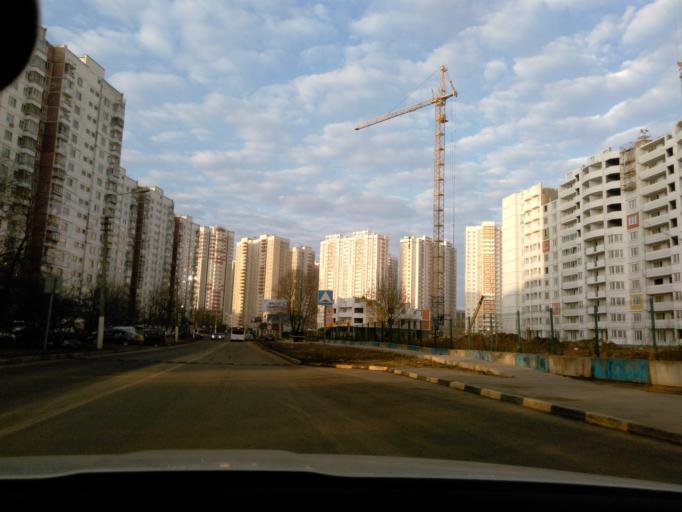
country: RU
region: Moscow
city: Khimki
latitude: 55.9061
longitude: 37.4059
